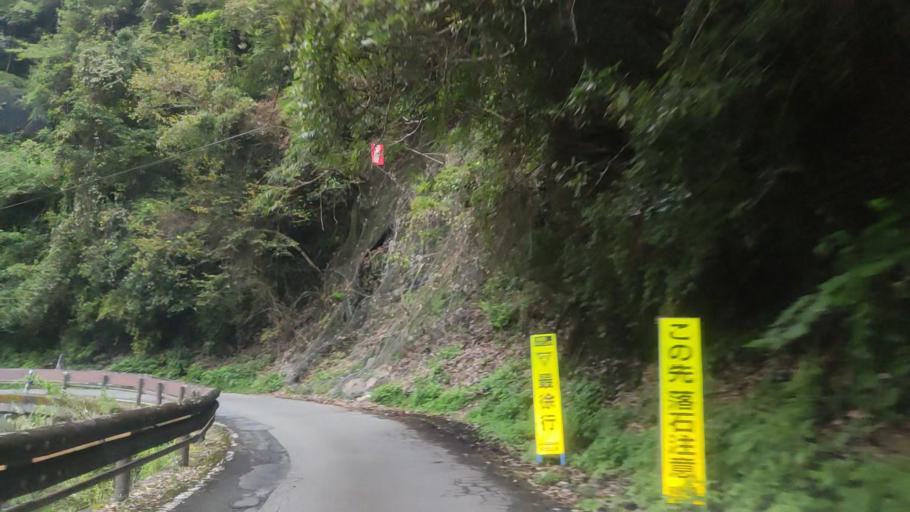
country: JP
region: Wakayama
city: Hashimoto
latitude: 34.2671
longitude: 135.6457
